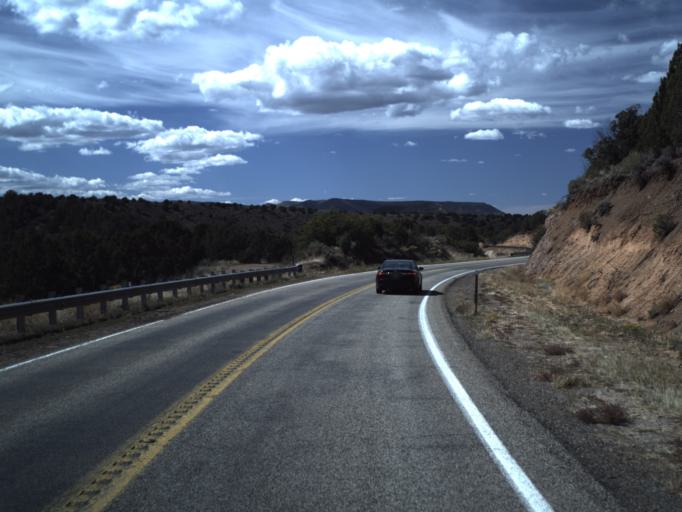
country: US
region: Utah
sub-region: Washington County
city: Enterprise
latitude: 37.5403
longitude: -113.6734
